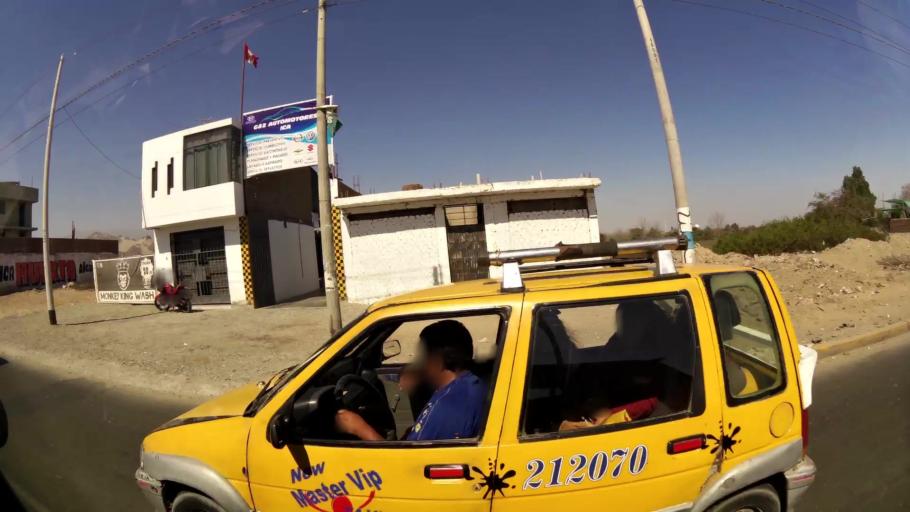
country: PE
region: Ica
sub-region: Provincia de Ica
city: La Tinguina
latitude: -14.0545
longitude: -75.7068
